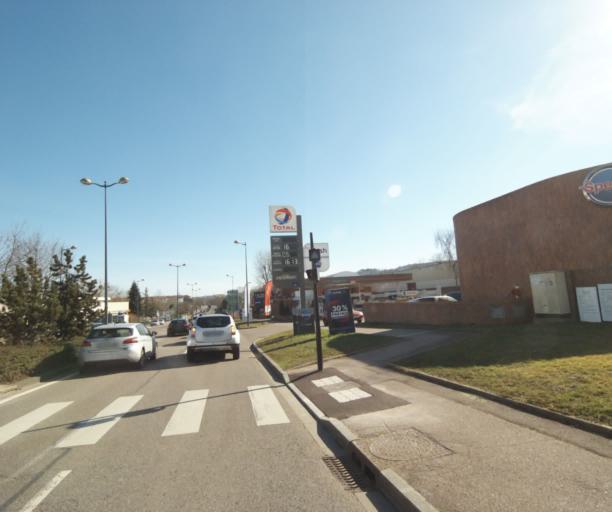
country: FR
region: Lorraine
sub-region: Departement de Meurthe-et-Moselle
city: Villers-les-Nancy
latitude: 48.6731
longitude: 6.1533
